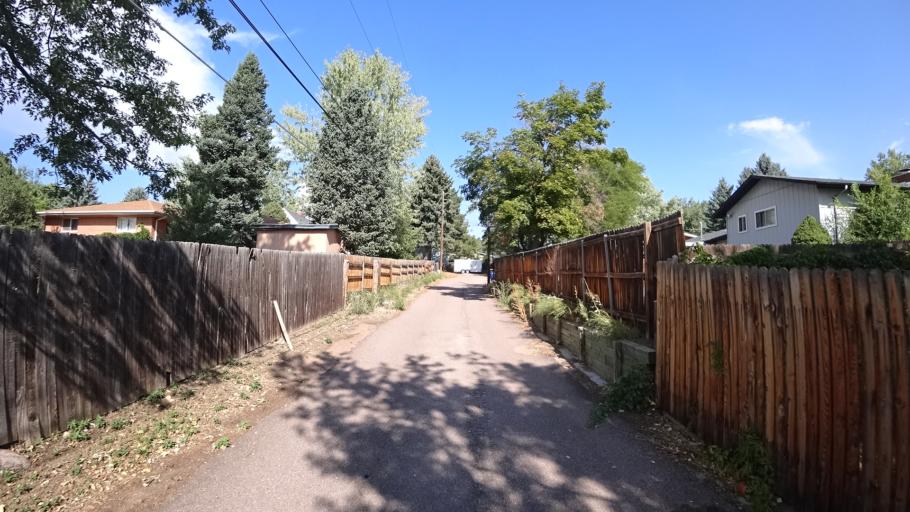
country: US
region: Colorado
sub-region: El Paso County
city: Colorado Springs
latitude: 38.8661
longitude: -104.7681
